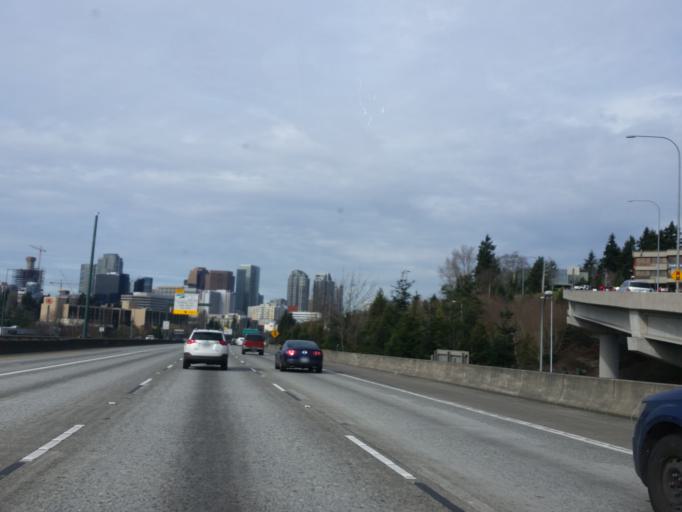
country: US
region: Washington
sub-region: King County
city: Bellevue
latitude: 47.6029
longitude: -122.1836
